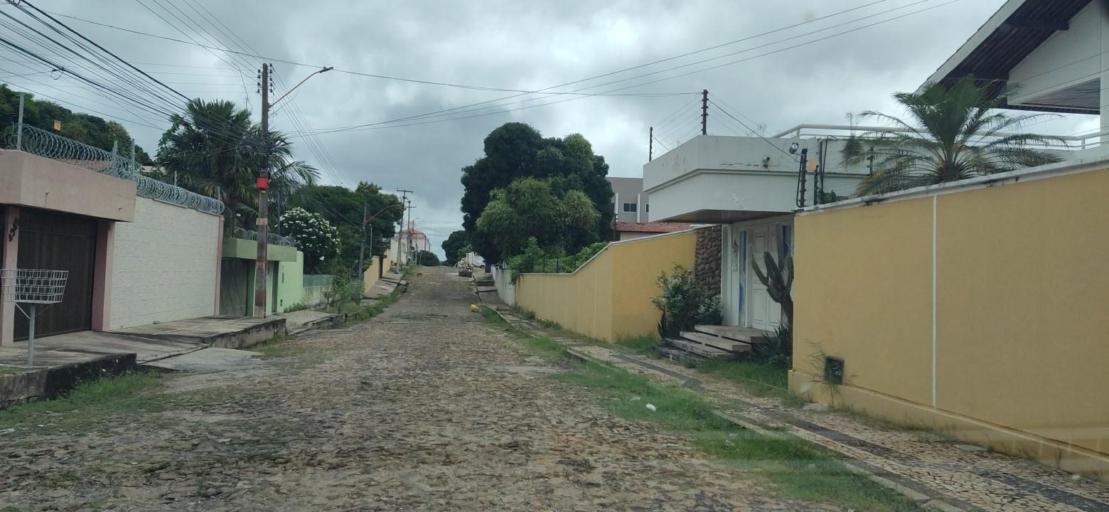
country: BR
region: Piaui
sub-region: Teresina
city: Teresina
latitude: -5.0729
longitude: -42.7613
